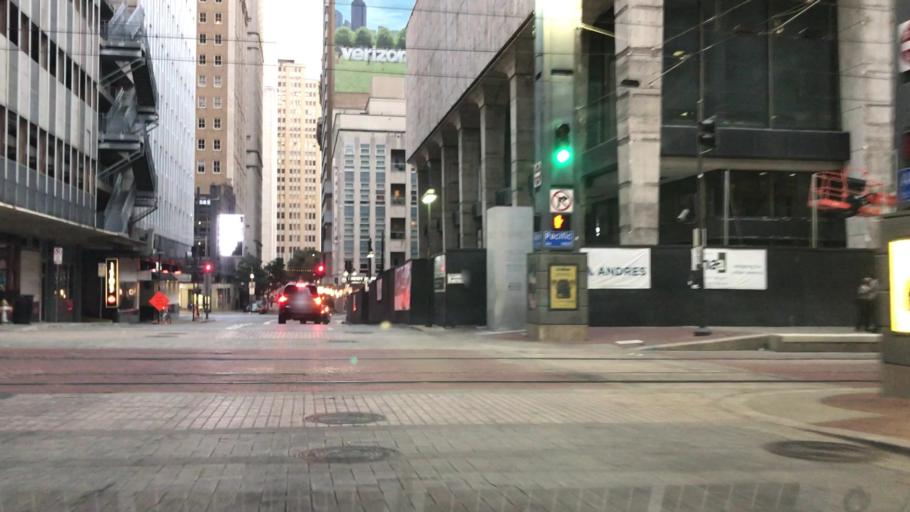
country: US
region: Texas
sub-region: Dallas County
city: Dallas
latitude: 32.7822
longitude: -96.8000
